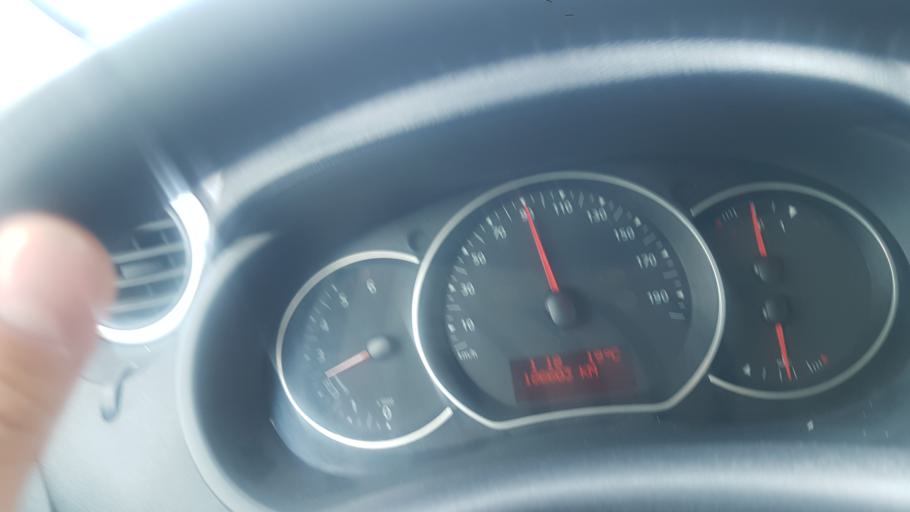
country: TR
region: Mersin
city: Yenice
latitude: 37.0674
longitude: 35.1718
